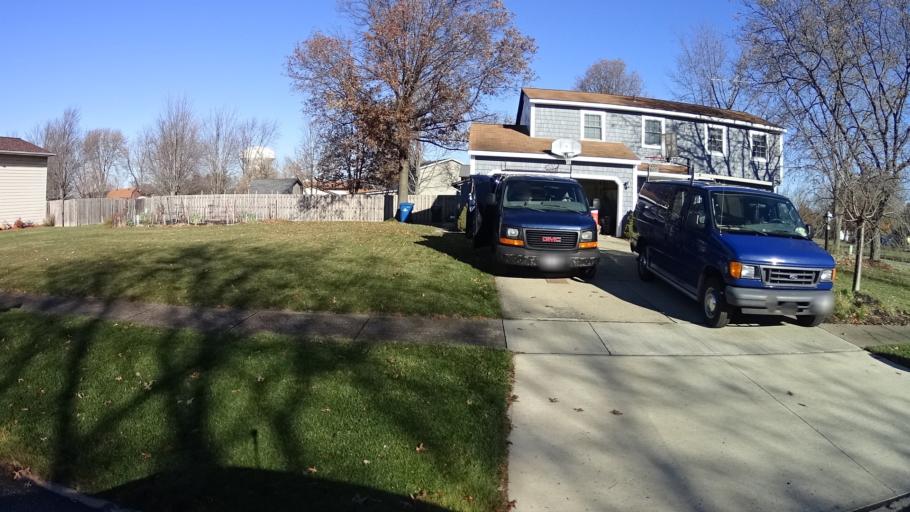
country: US
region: Ohio
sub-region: Lorain County
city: North Ridgeville
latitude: 41.4149
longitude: -82.0154
